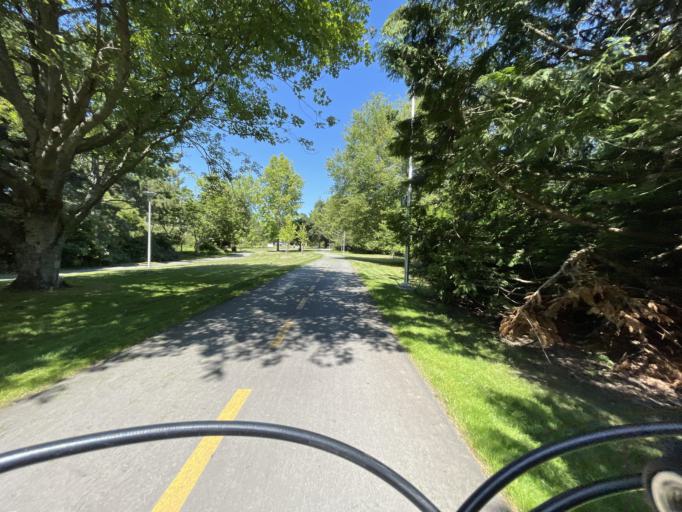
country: CA
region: British Columbia
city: Oak Bay
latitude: 48.4614
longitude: -123.3138
